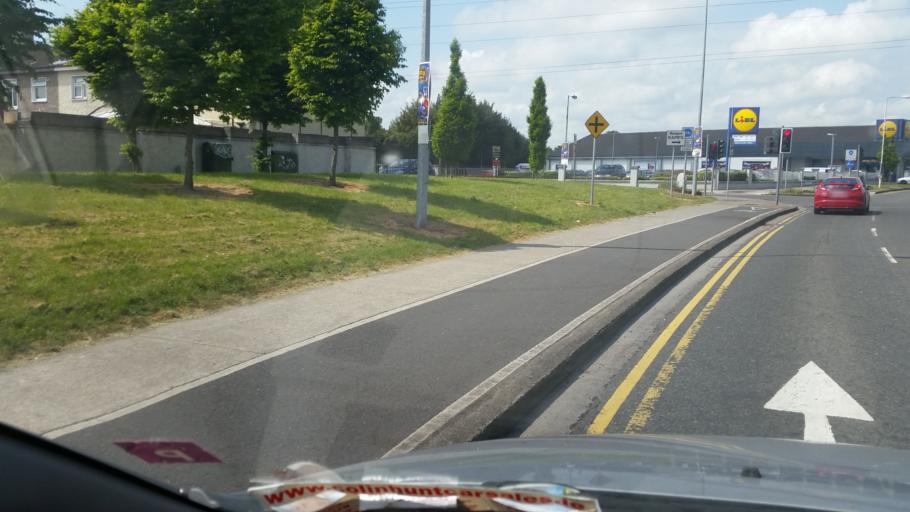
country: IE
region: Leinster
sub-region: Fingal County
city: Blanchardstown
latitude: 53.3950
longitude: -6.3999
